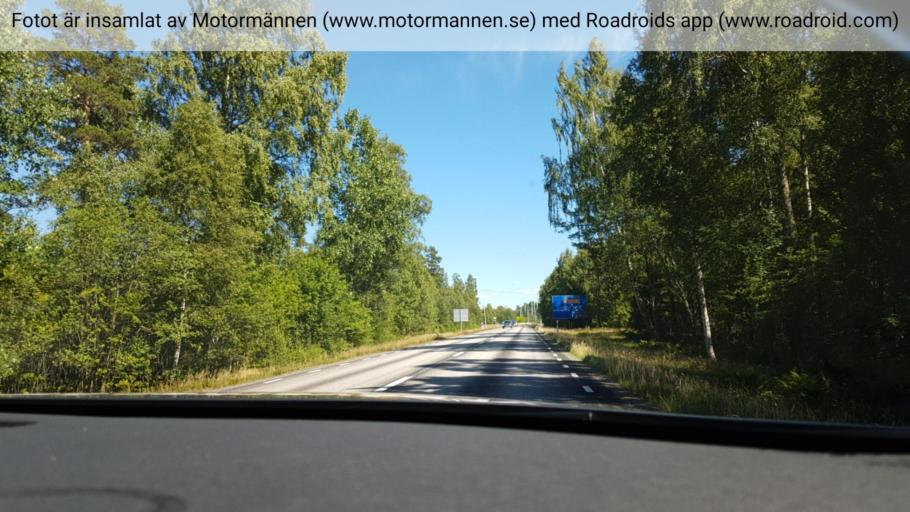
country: SE
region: Joenkoeping
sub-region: Gnosjo Kommun
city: Hillerstorp
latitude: 57.3170
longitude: 13.9042
